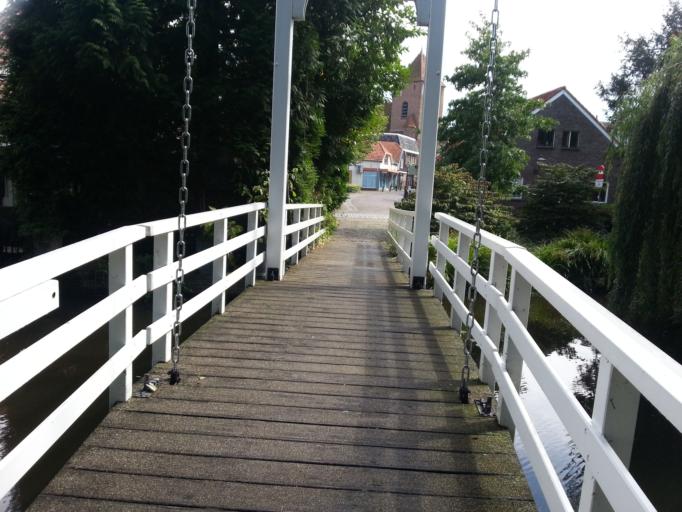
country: NL
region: Gelderland
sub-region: Berkelland
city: Borculo
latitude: 52.1159
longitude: 6.5220
